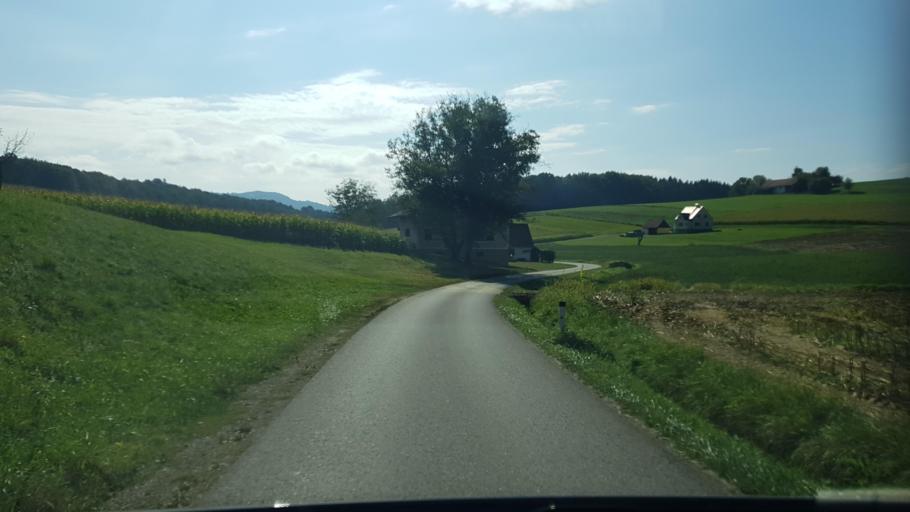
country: AT
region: Styria
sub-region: Politischer Bezirk Deutschlandsberg
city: Wettmannstatten
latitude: 46.8220
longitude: 15.3719
